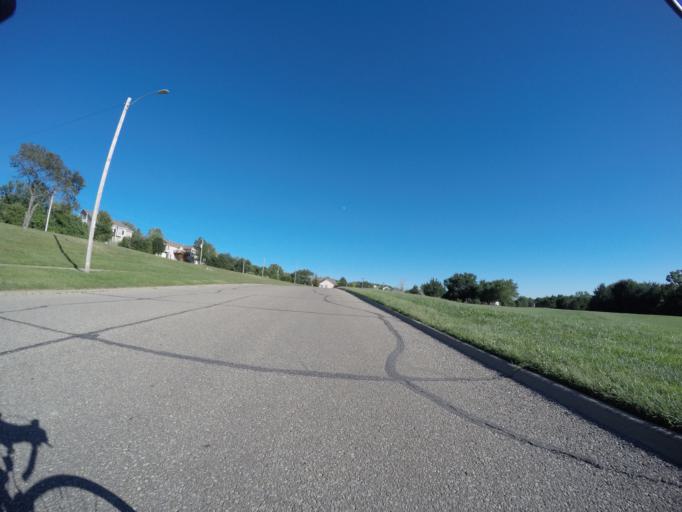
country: US
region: Kansas
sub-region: Riley County
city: Manhattan
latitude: 39.2060
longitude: -96.6319
